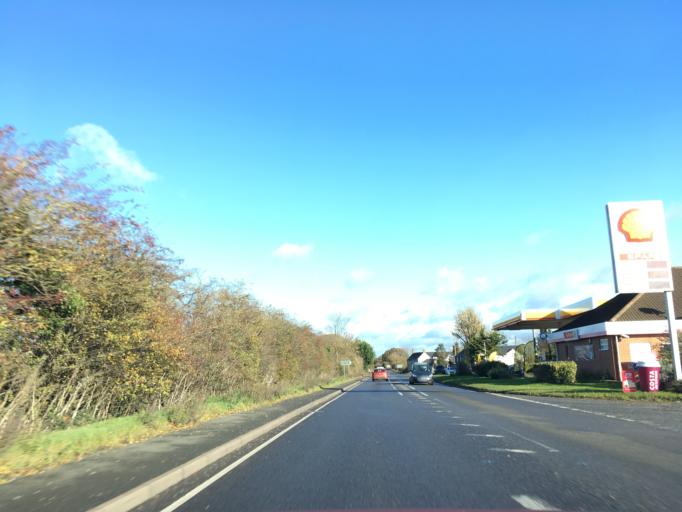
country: GB
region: England
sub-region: Worcestershire
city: Evesham
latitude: 52.0299
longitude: -1.9998
